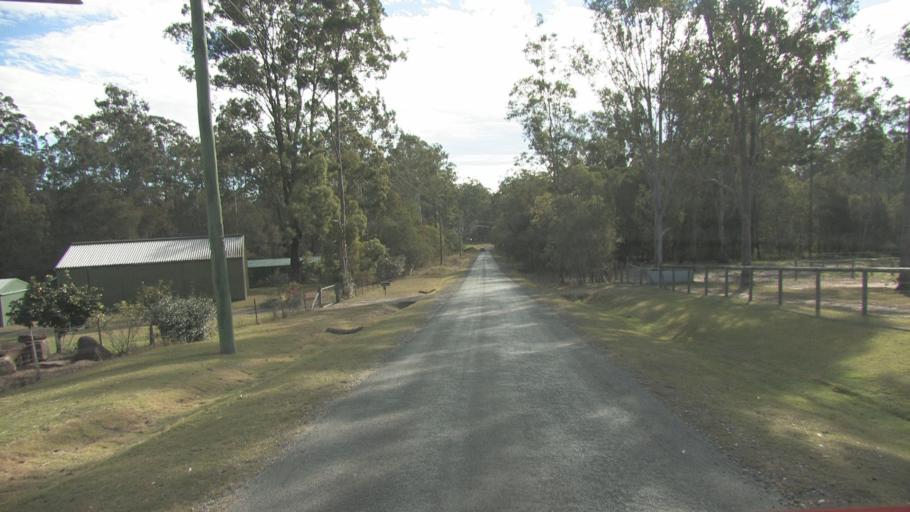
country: AU
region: Queensland
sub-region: Logan
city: Cedar Vale
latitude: -27.8279
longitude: 153.0692
